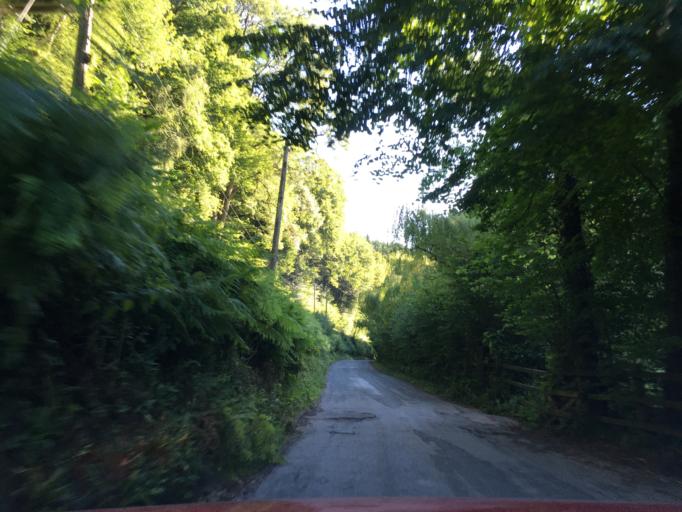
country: GB
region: Wales
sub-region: Monmouthshire
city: Tintern
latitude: 51.6970
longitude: -2.7189
